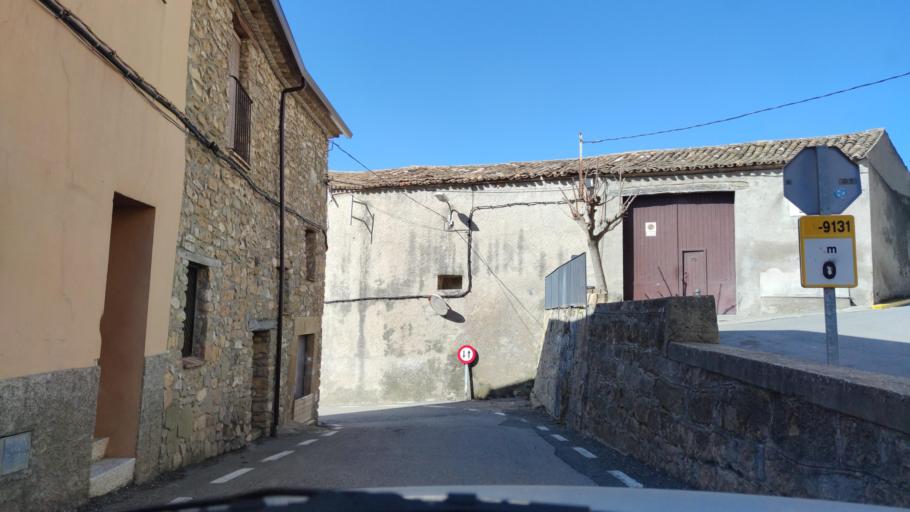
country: ES
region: Catalonia
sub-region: Provincia de Lleida
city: Artesa de Segre
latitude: 41.9943
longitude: 1.0232
